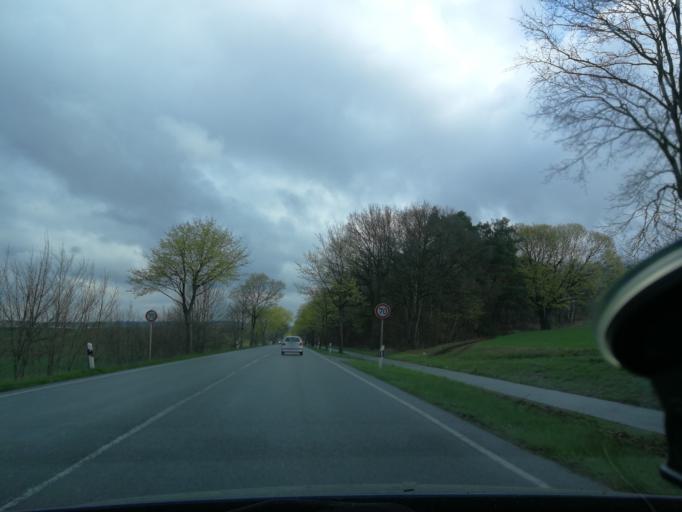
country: DE
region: Lower Saxony
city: Buchholz in der Nordheide
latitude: 53.3358
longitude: 9.8423
